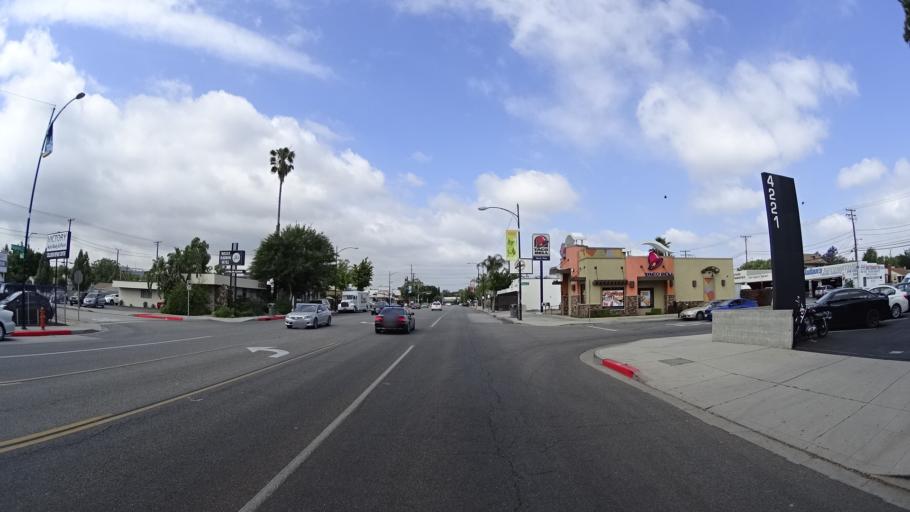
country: US
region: California
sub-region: Los Angeles County
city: North Hollywood
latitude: 34.1659
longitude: -118.3529
